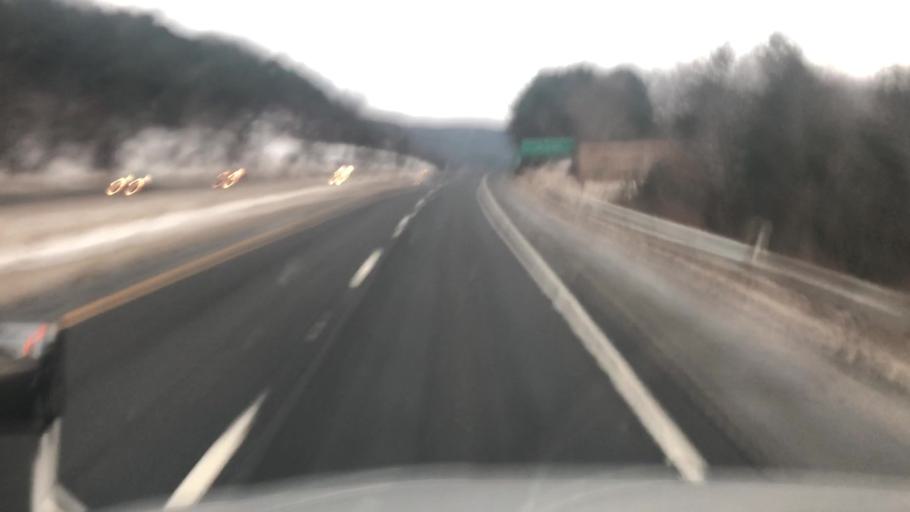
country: US
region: Pennsylvania
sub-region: Susquehanna County
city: Hallstead
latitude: 41.9751
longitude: -75.7416
